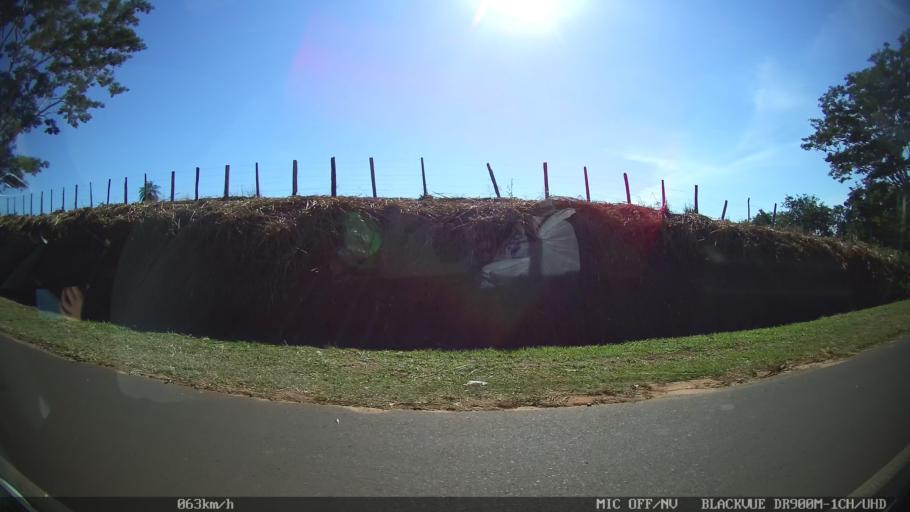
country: BR
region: Sao Paulo
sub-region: Olimpia
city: Olimpia
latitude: -20.7267
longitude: -48.8653
